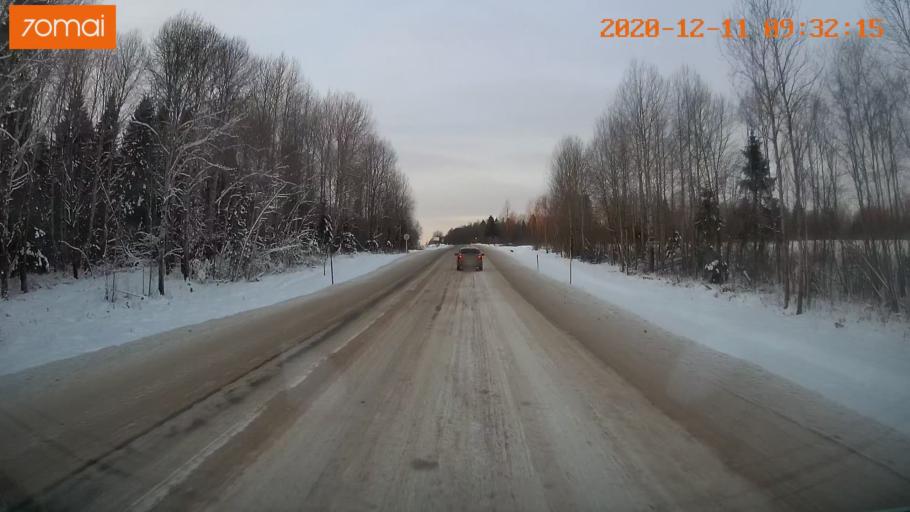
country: RU
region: Vologda
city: Vologda
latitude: 59.1242
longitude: 39.9713
